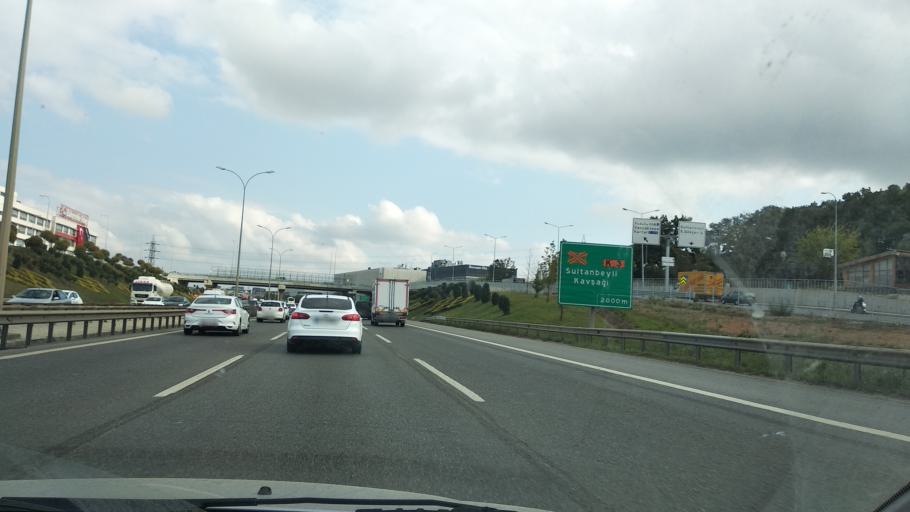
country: TR
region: Istanbul
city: Samandira
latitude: 40.9779
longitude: 29.2237
